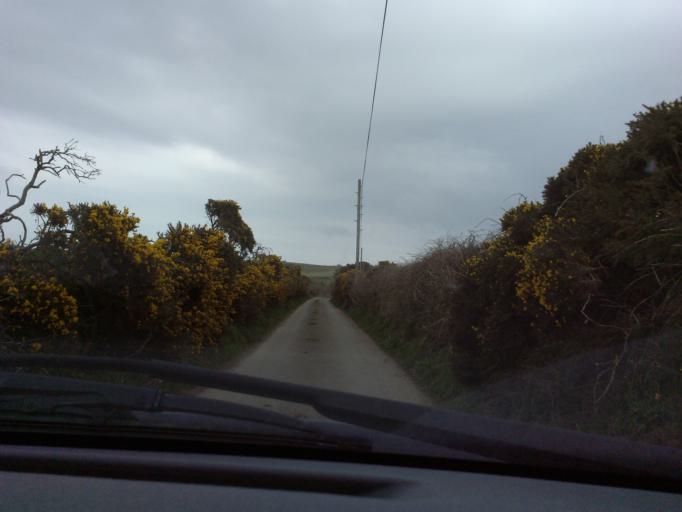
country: GB
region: England
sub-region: Cornwall
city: Saint Just
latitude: 50.1063
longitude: -5.6605
